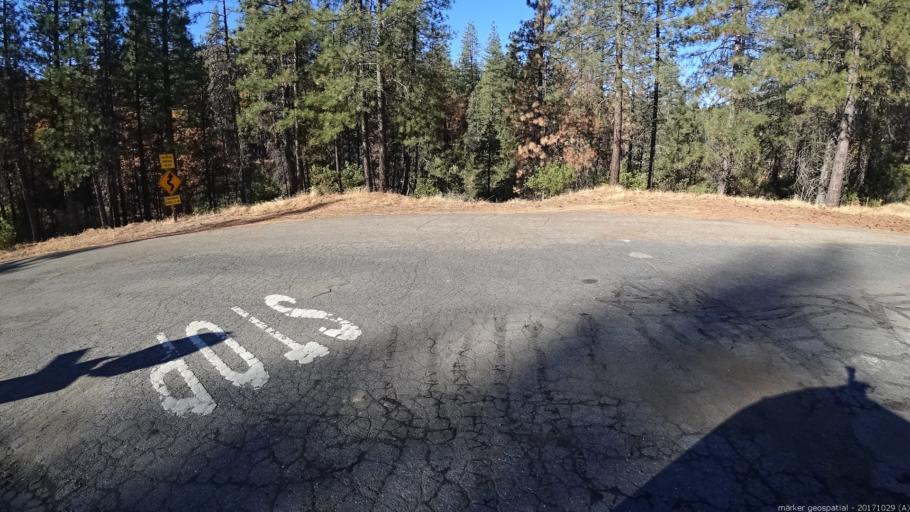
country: US
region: California
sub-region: Trinity County
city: Hayfork
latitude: 40.3679
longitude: -122.9719
